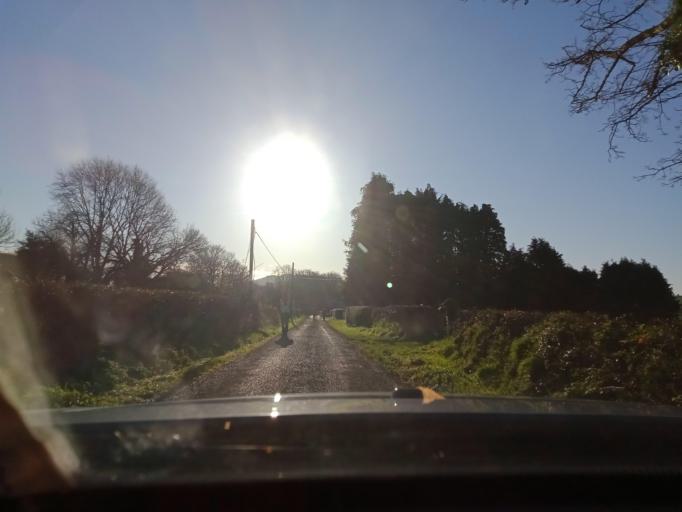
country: IE
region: Munster
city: Carrick-on-Suir
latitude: 52.4380
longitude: -7.4171
